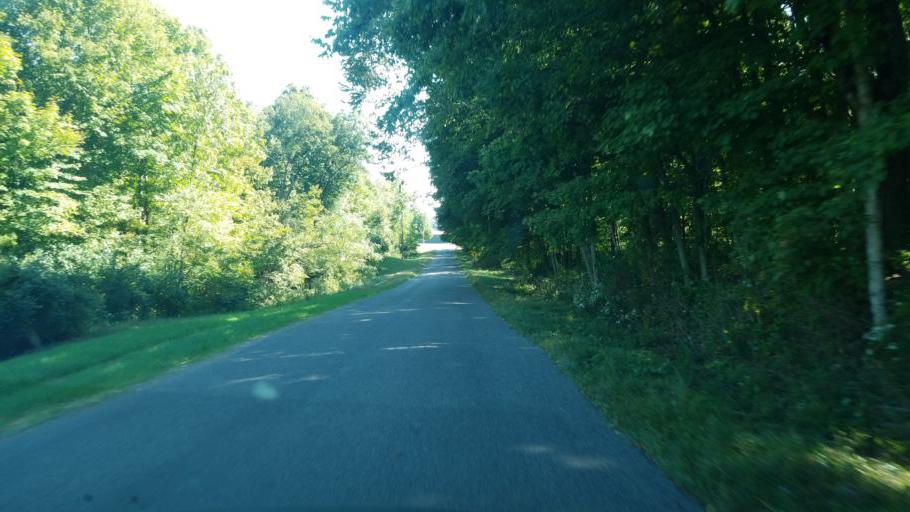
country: US
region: Ohio
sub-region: Champaign County
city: North Lewisburg
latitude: 40.1785
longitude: -83.6146
